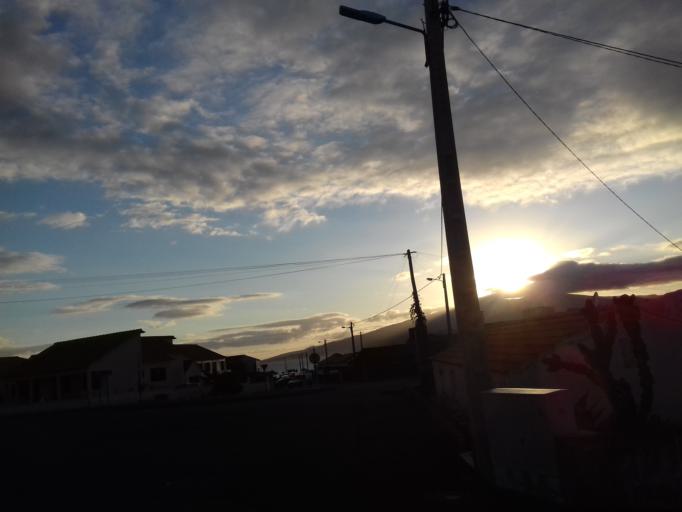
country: PT
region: Azores
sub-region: Madalena
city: Madalena
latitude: 38.5331
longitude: -28.5312
